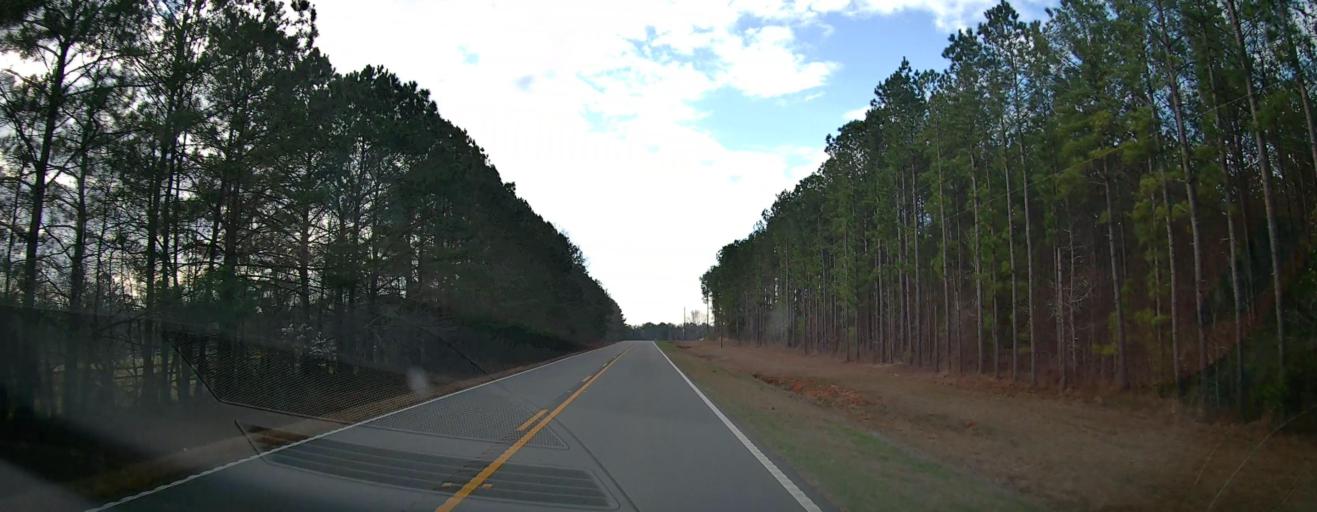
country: US
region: Georgia
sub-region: Harris County
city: Hamilton
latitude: 32.6951
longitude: -84.7982
